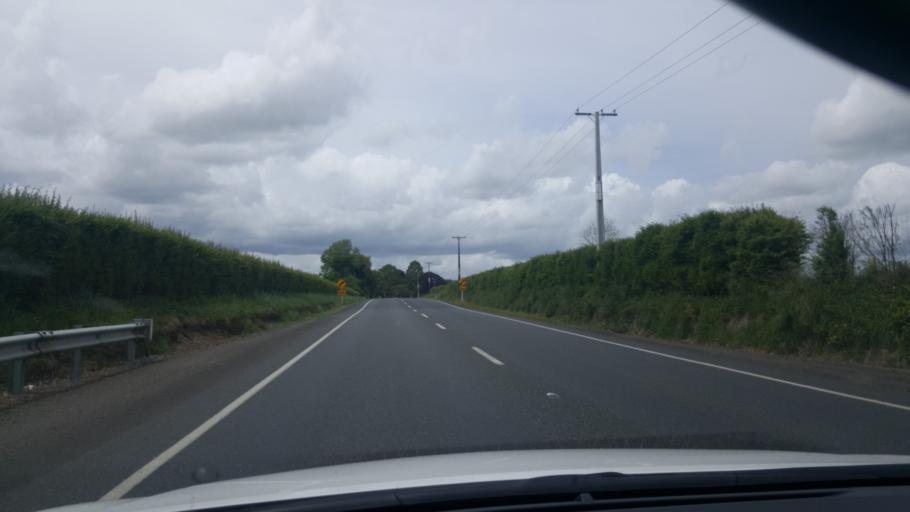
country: NZ
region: Waikato
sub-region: Matamata-Piako District
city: Matamata
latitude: -37.8799
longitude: 175.7498
